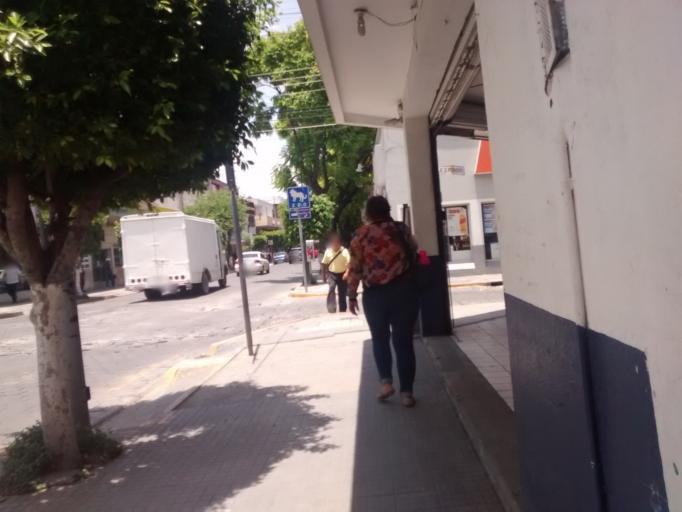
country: MX
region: Puebla
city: Tehuacan
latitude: 18.4652
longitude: -97.3941
